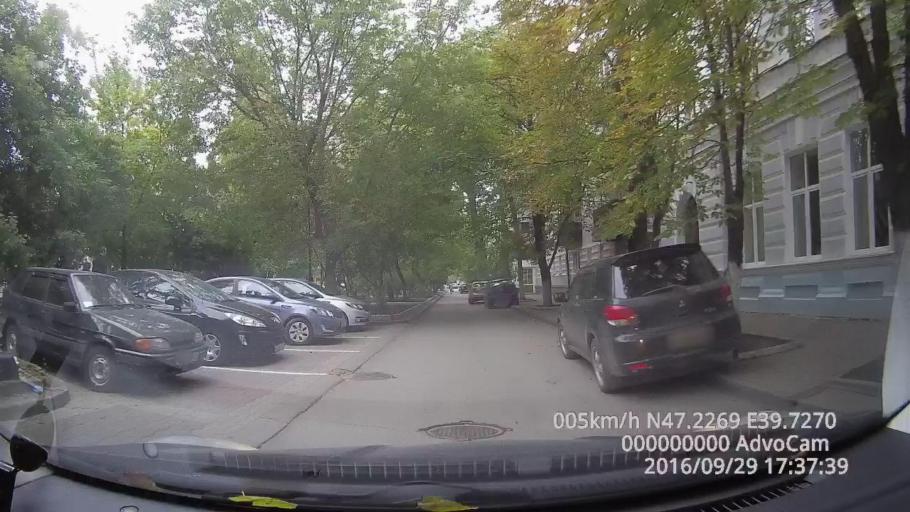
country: RU
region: Rostov
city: Rostov-na-Donu
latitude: 47.2269
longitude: 39.7270
